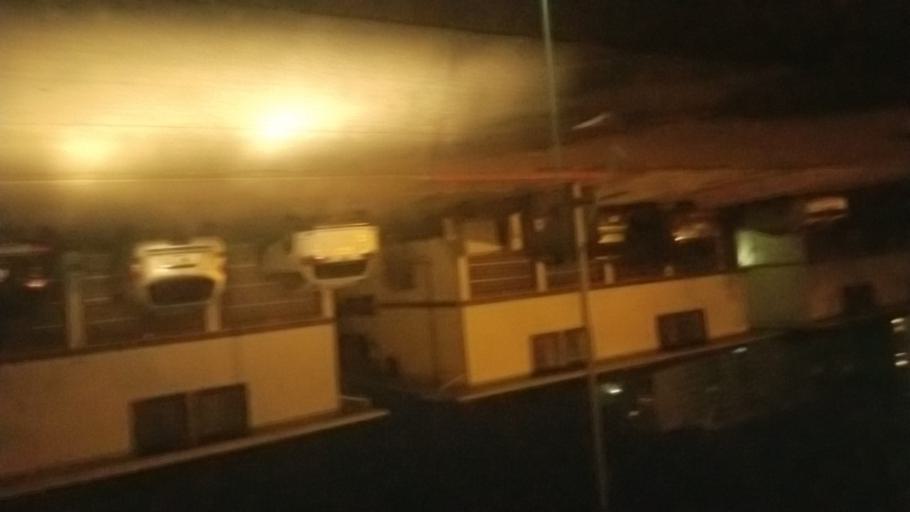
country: US
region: Maryland
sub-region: Worcester County
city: Ocean City
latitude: 38.4191
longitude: -75.0586
